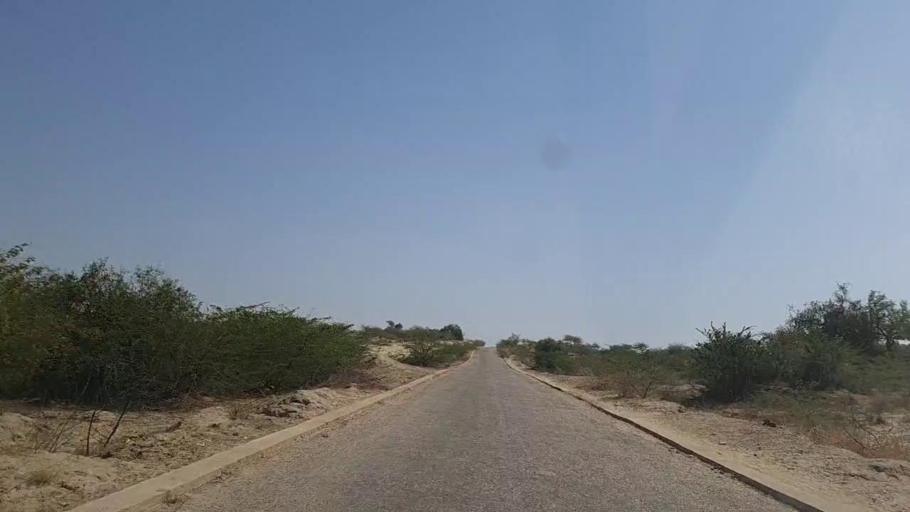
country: PK
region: Sindh
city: Diplo
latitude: 24.5147
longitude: 69.3802
